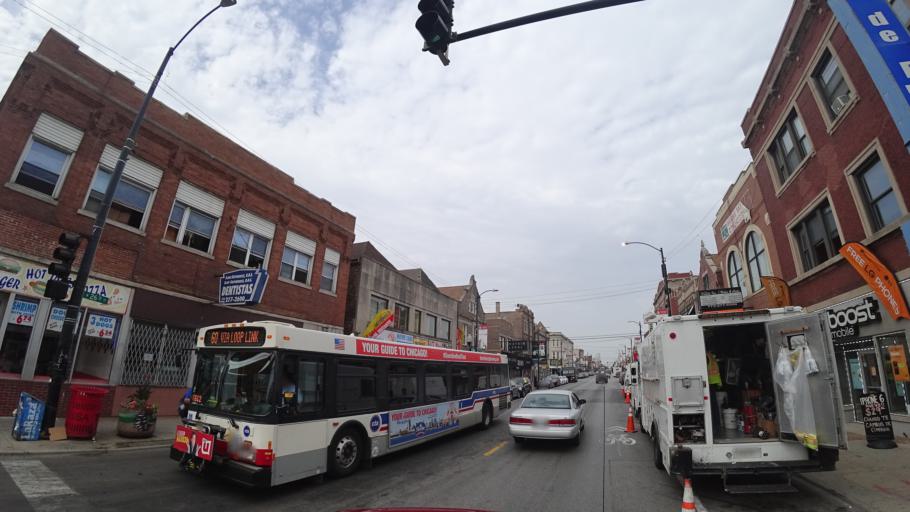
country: US
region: Illinois
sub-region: Cook County
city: Cicero
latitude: 41.8445
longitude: -87.7150
